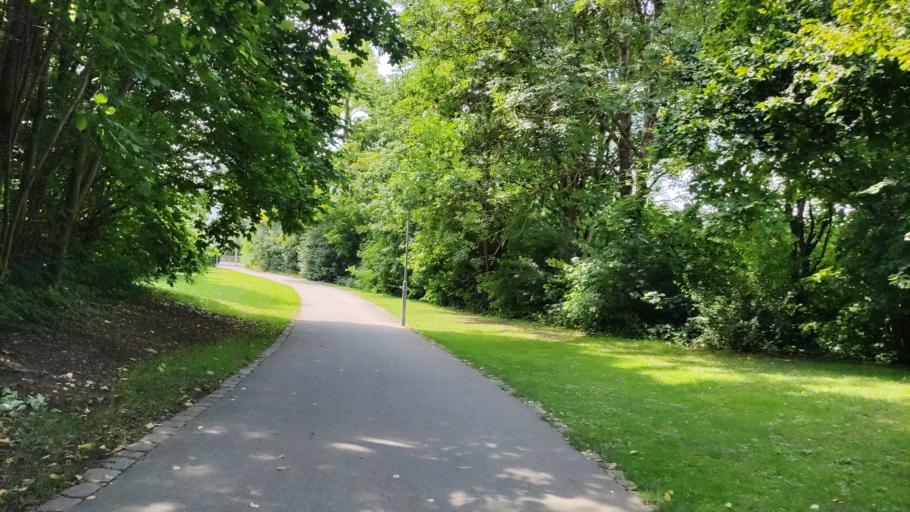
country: DE
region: Bavaria
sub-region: Swabia
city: Konigsbrunn
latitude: 48.2714
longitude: 10.8952
